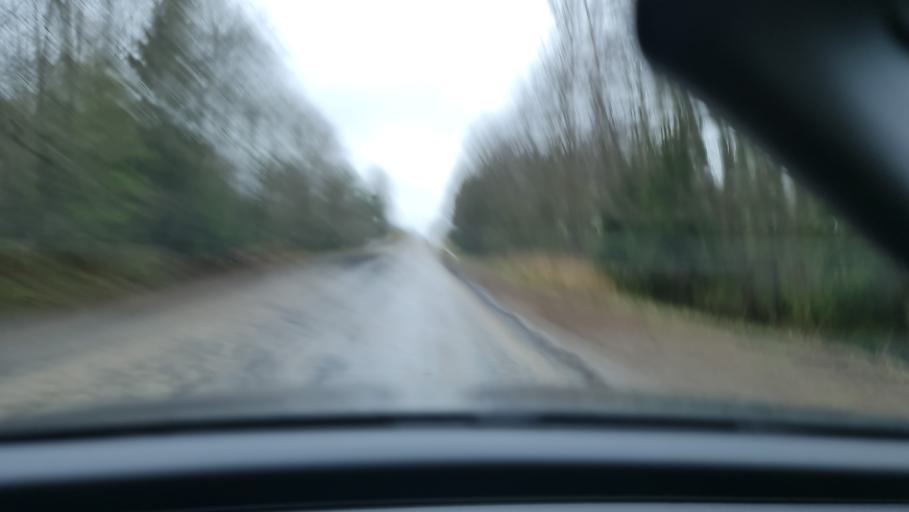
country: RU
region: Novgorod
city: Valday
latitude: 58.0360
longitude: 32.8861
